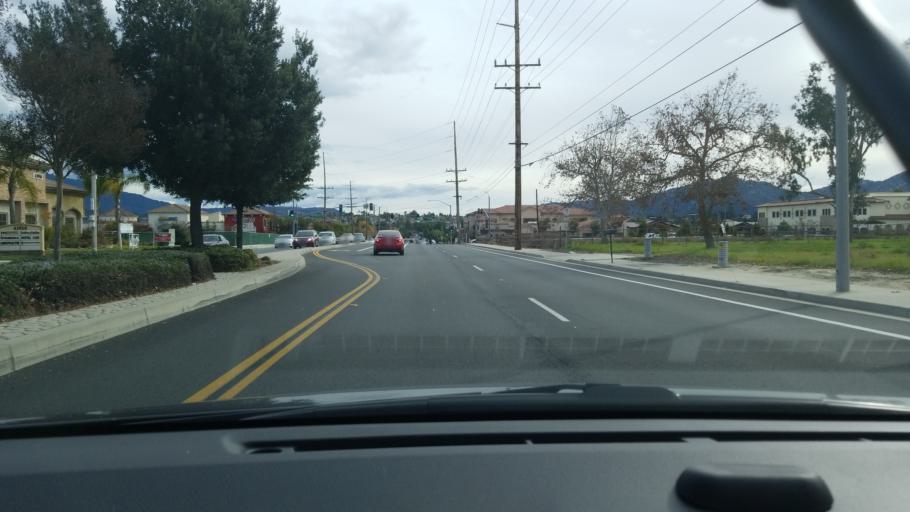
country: US
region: California
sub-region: Riverside County
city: Temecula
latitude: 33.4854
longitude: -117.1035
